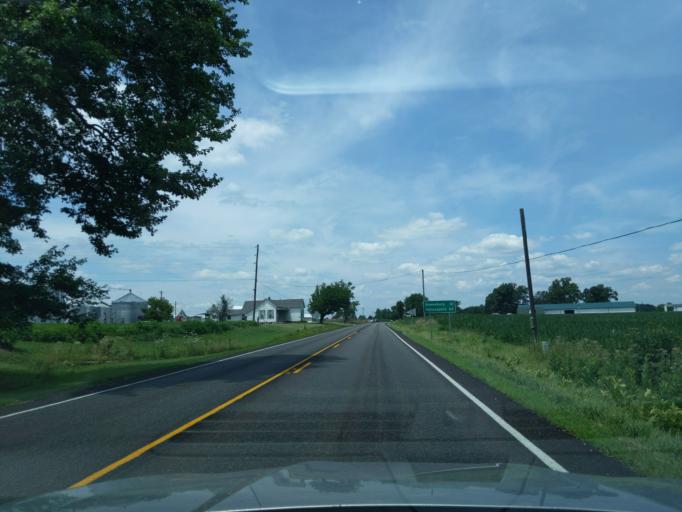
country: US
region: Indiana
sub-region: Ripley County
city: Osgood
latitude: 39.2092
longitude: -85.3312
